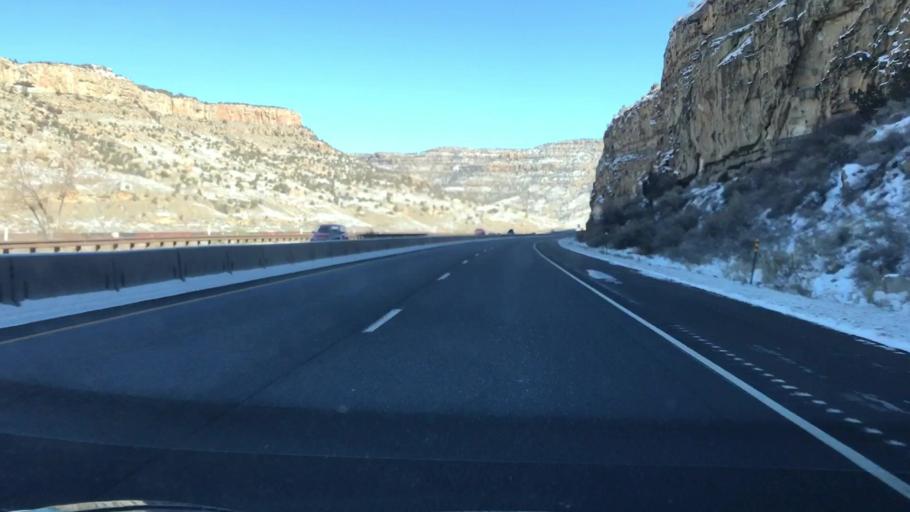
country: US
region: Colorado
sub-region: Mesa County
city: Palisade
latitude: 39.2032
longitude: -108.2657
